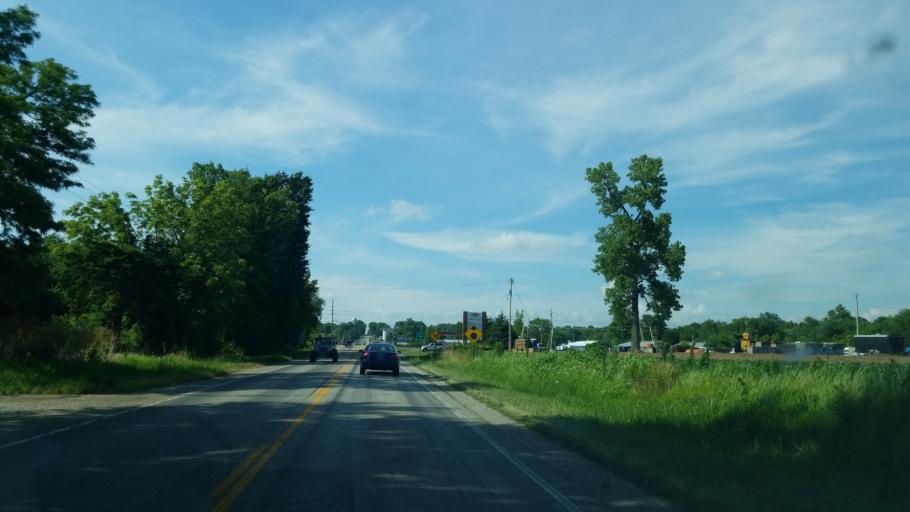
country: US
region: Illinois
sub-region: Saint Clair County
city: Lebanon
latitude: 38.5924
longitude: -89.8077
